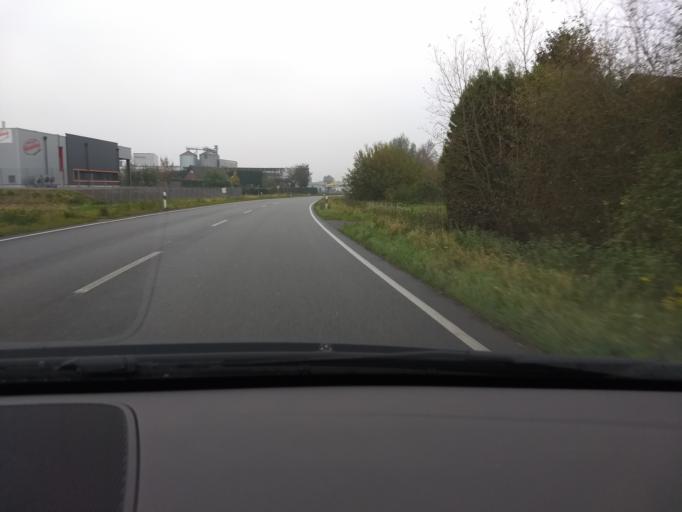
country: DE
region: North Rhine-Westphalia
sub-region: Regierungsbezirk Munster
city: Sudlohn
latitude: 51.9383
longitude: 6.8209
